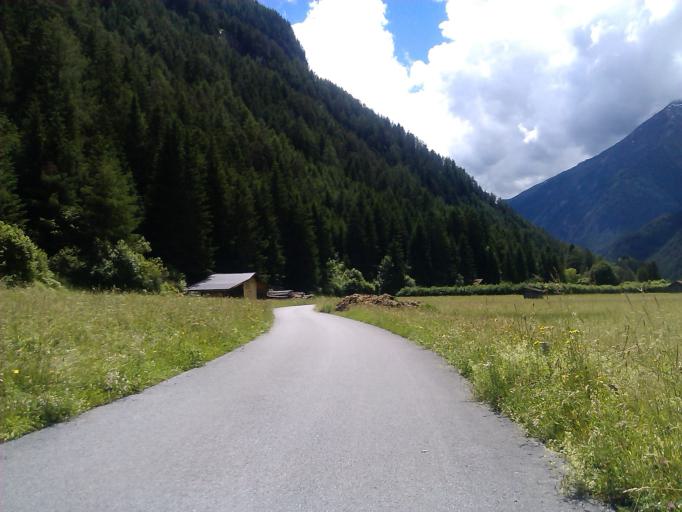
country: AT
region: Tyrol
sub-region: Politischer Bezirk Landeck
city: Pfunds
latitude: 46.9603
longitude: 10.5286
